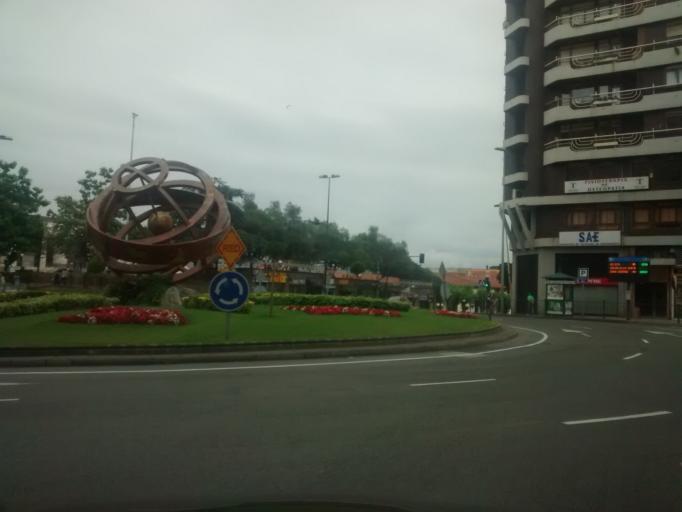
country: ES
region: Cantabria
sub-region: Provincia de Cantabria
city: Santander
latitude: 43.4587
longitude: -3.8265
